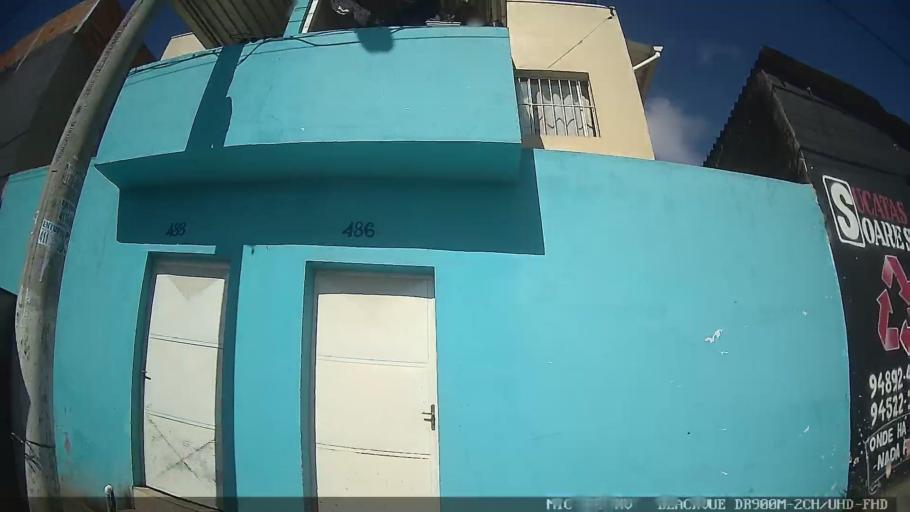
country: BR
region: Sao Paulo
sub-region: Poa
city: Poa
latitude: -23.5065
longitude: -46.3381
